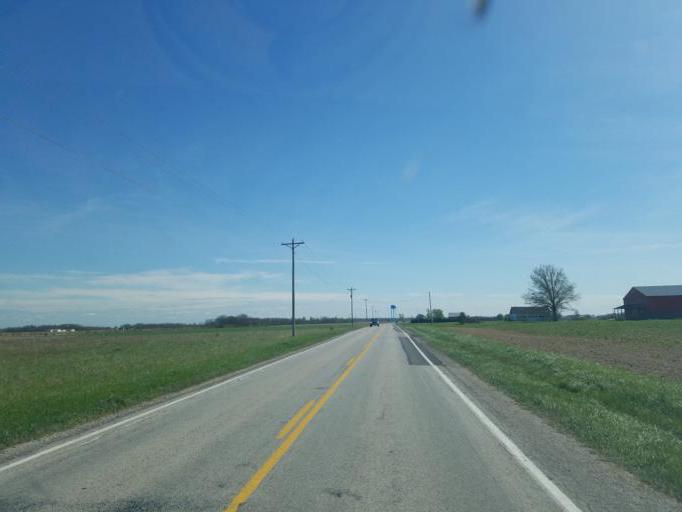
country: US
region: Ohio
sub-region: Huron County
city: Bellevue
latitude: 41.1792
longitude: -82.8373
